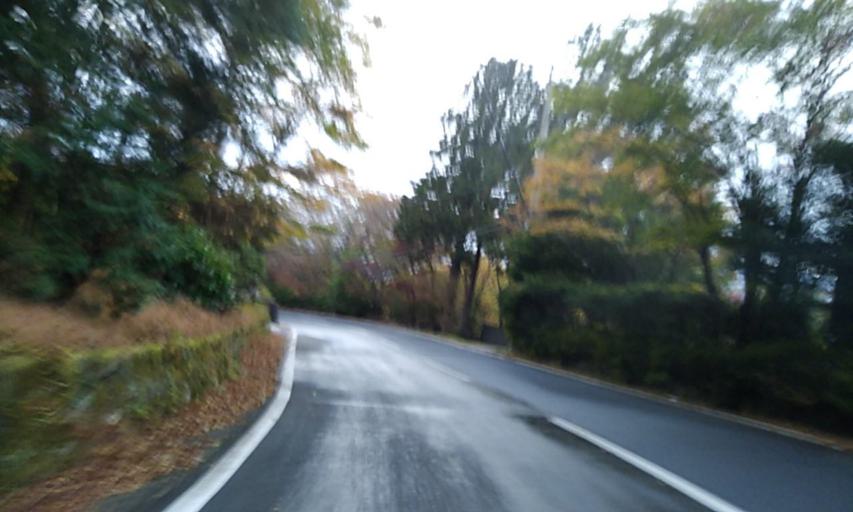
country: JP
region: Kanagawa
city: Hakone
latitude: 35.2468
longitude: 139.0067
